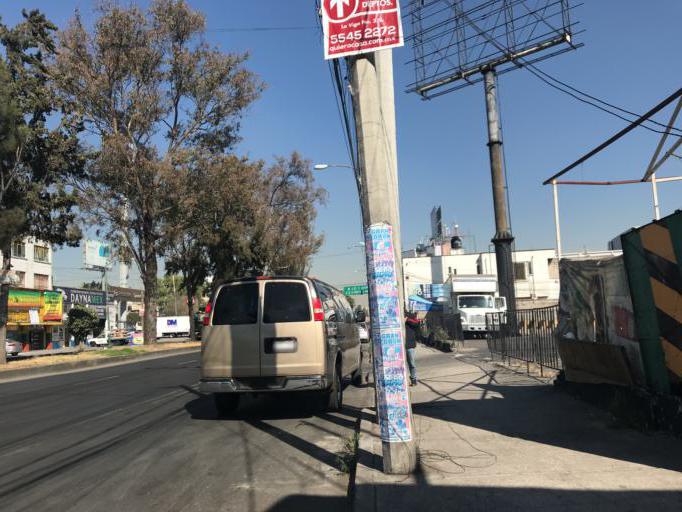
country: MX
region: Mexico City
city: Colonia Nativitas
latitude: 19.4032
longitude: -99.1254
